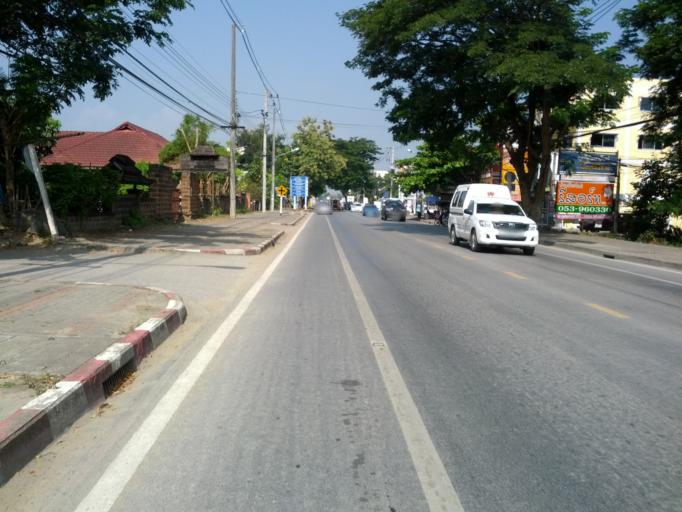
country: TH
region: Chiang Mai
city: San Kamphaeng
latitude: 18.7688
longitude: 99.0723
